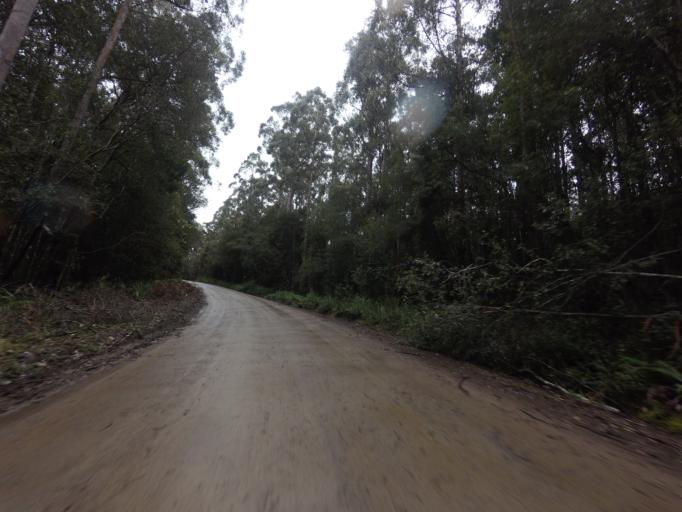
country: AU
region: Tasmania
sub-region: Huon Valley
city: Geeveston
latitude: -43.4990
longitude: 146.8792
